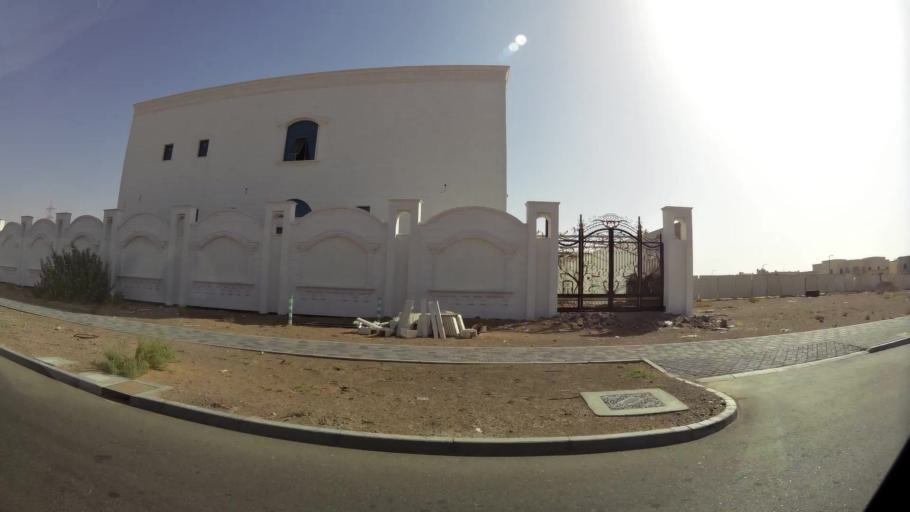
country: OM
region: Al Buraimi
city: Al Buraymi
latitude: 24.3597
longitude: 55.7894
